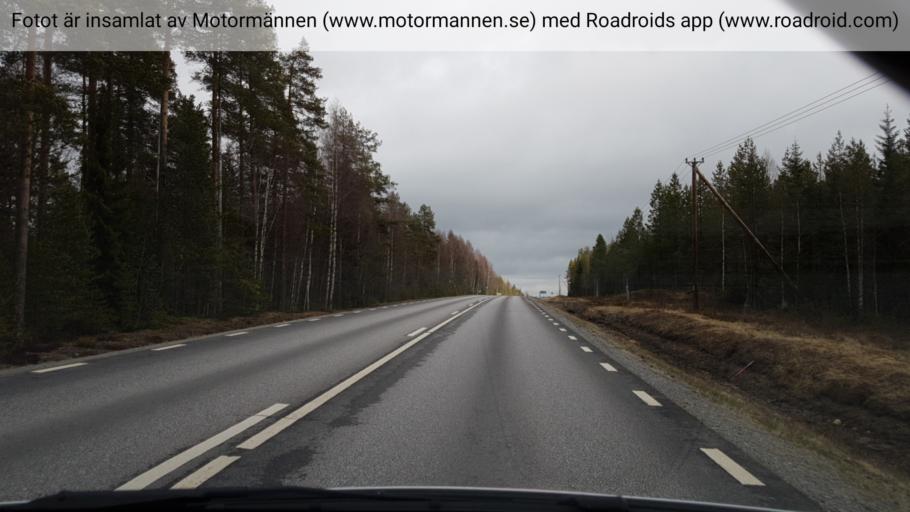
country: SE
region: Vaesterbotten
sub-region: Vannas Kommun
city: Vaennaes
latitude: 63.9264
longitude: 19.5633
